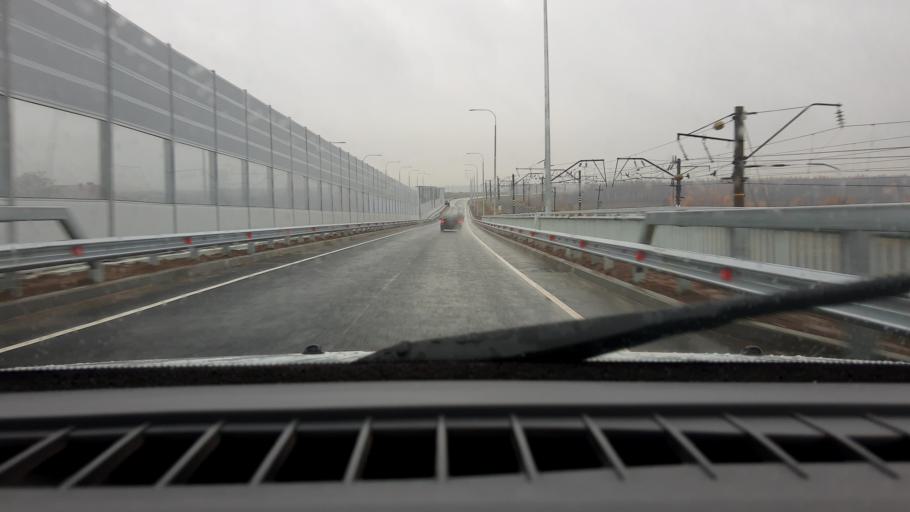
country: RU
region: Nizjnij Novgorod
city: Neklyudovo
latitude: 56.3990
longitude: 43.9818
